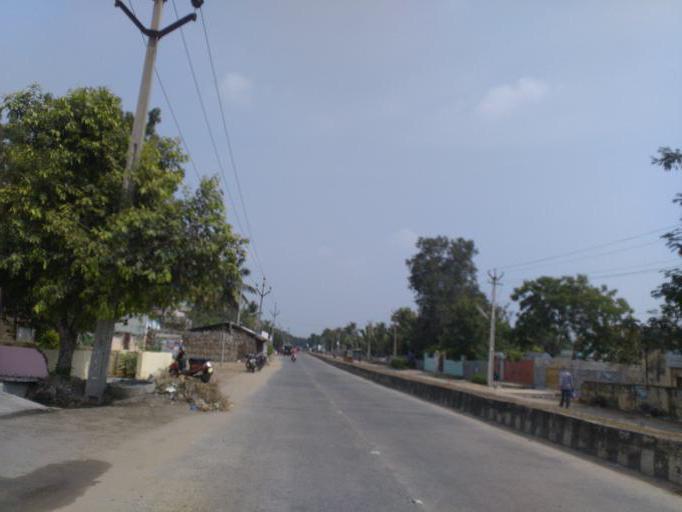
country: IN
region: Andhra Pradesh
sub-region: Prakasam
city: Chirala
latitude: 15.8432
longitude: 80.3759
